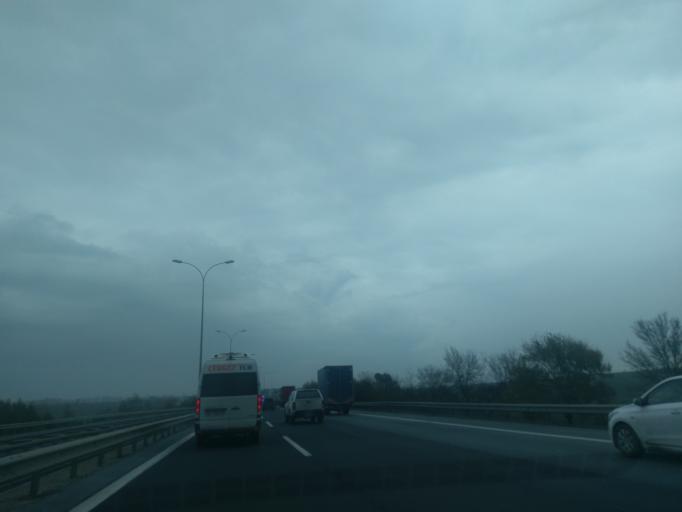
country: TR
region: Istanbul
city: Tepecik
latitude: 41.1065
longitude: 28.5727
